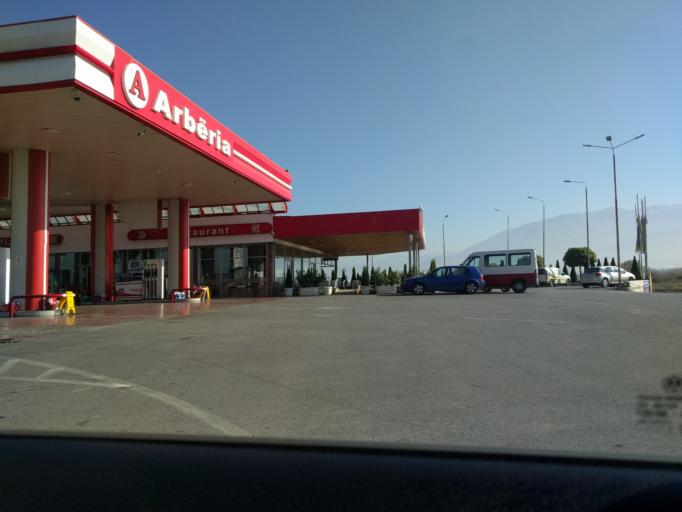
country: XK
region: Prizren
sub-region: Prizren
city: Prizren
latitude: 42.2478
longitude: 20.7206
